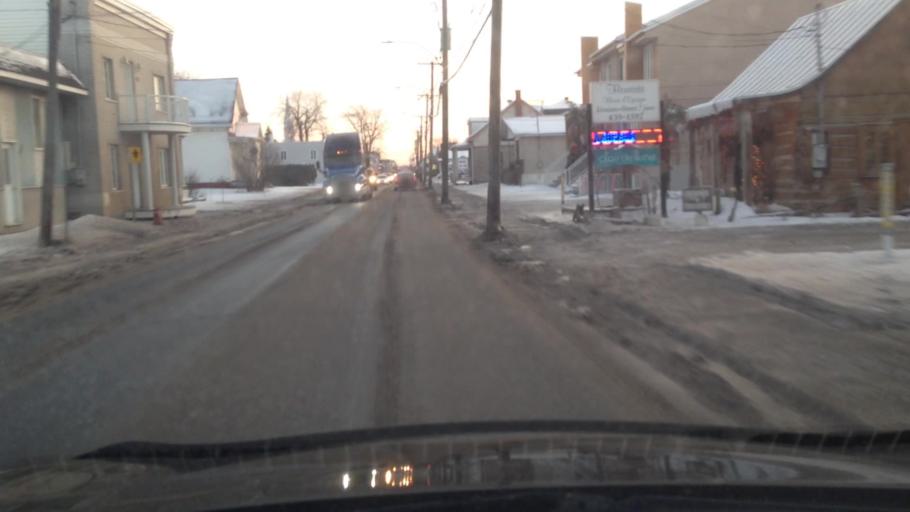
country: CA
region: Quebec
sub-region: Lanaudiere
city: Saint-Lin-Laurentides
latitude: 45.8582
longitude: -73.7571
